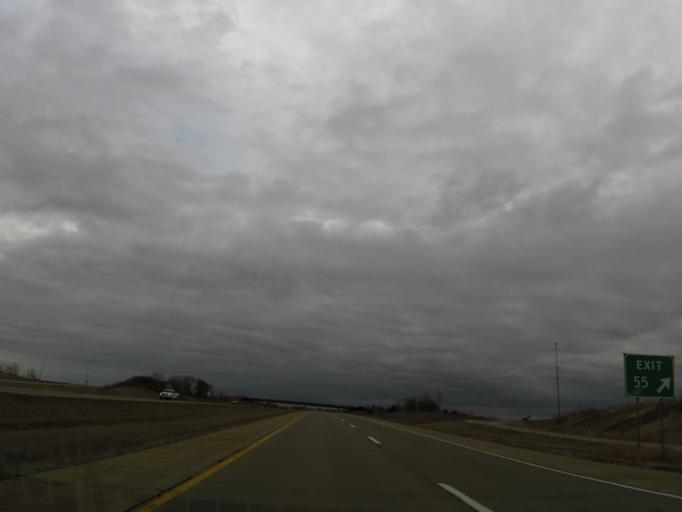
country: US
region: Iowa
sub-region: Buchanan County
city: Jesup
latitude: 42.3555
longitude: -92.0692
